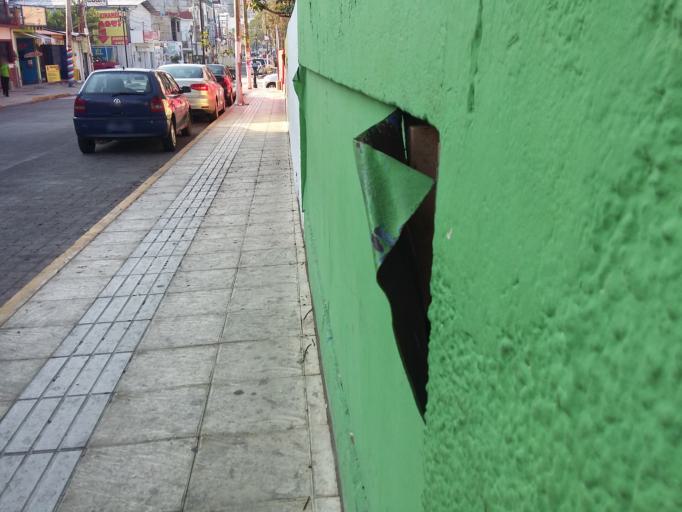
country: MX
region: Guerrero
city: Chilpancingo de los Bravos
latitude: 17.5480
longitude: -99.4990
